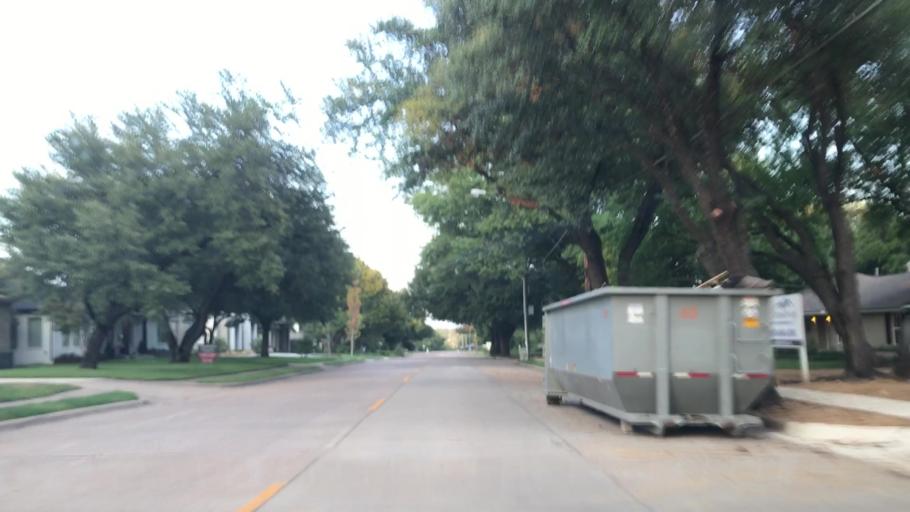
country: US
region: Texas
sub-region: Dallas County
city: University Park
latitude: 32.9008
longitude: -96.7777
